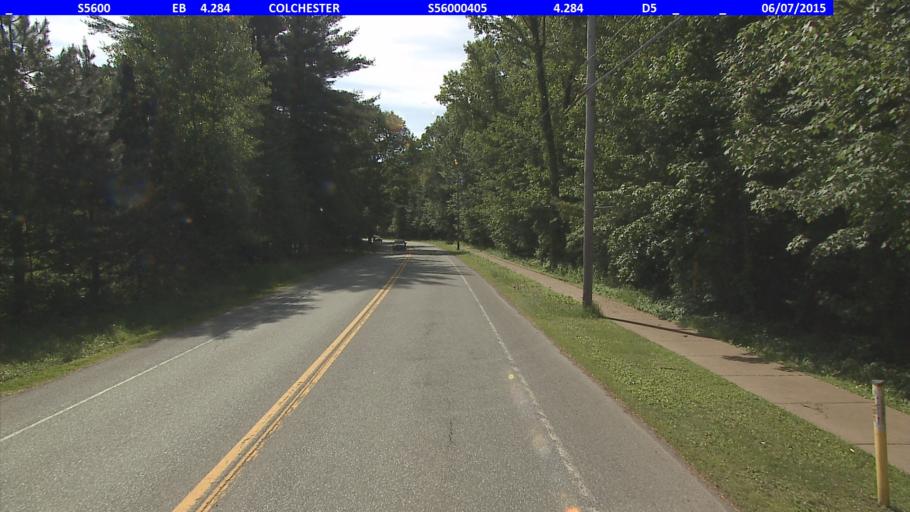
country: US
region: Vermont
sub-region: Chittenden County
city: Winooski
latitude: 44.5324
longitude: -73.2022
